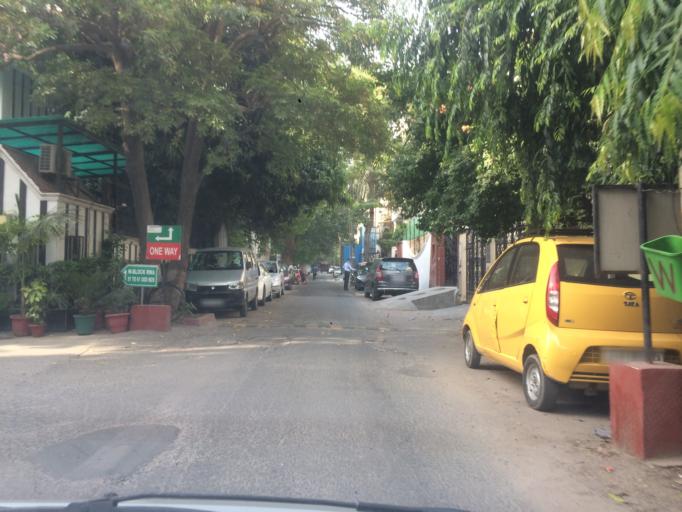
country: IN
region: NCT
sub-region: New Delhi
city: New Delhi
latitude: 28.5535
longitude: 77.2329
